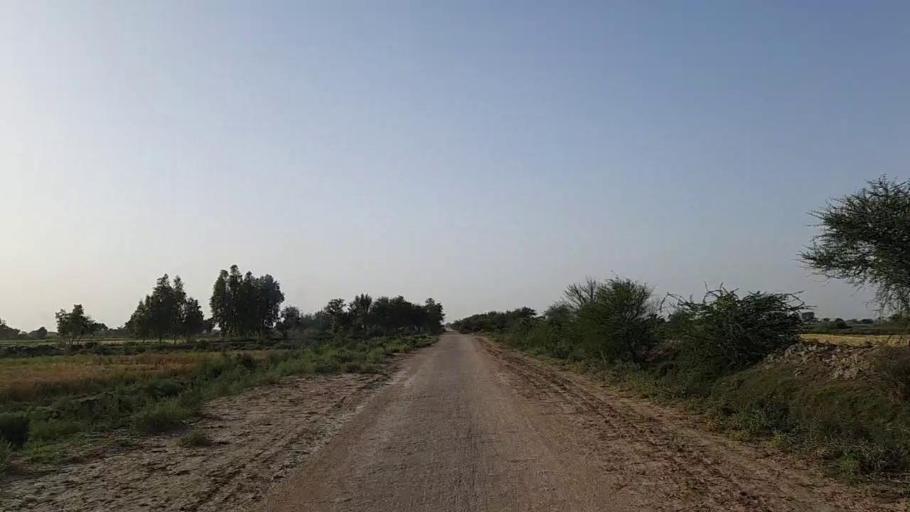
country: PK
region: Sindh
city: Jati
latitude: 24.3274
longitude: 68.1620
